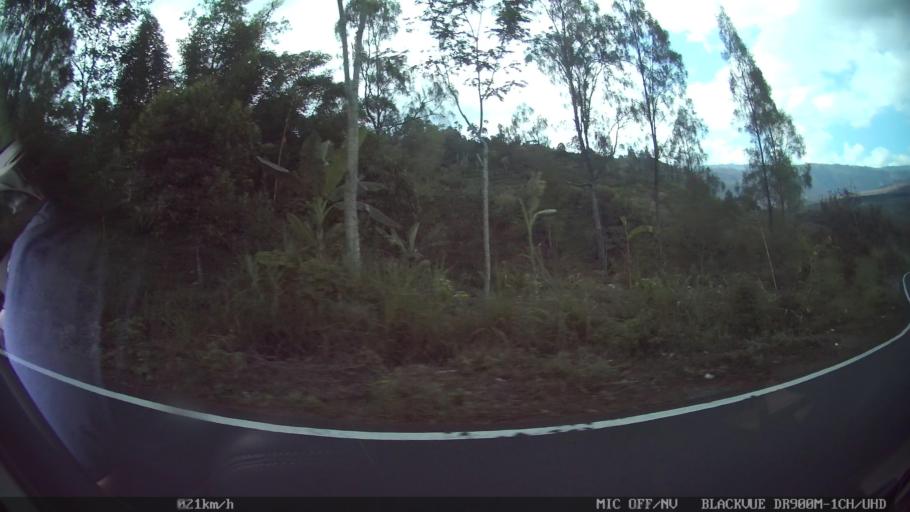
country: ID
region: Bali
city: Banjar Kedisan
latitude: -8.2586
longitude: 115.3485
